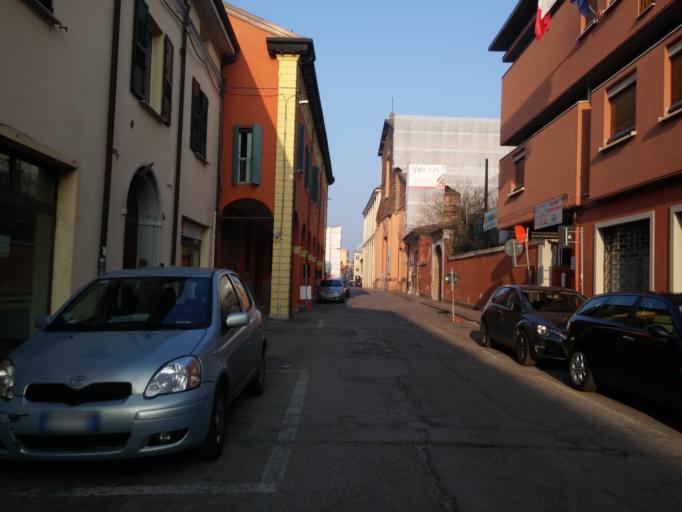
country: IT
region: Emilia-Romagna
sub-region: Provincia di Ferrara
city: Cento
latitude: 44.7275
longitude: 11.2879
